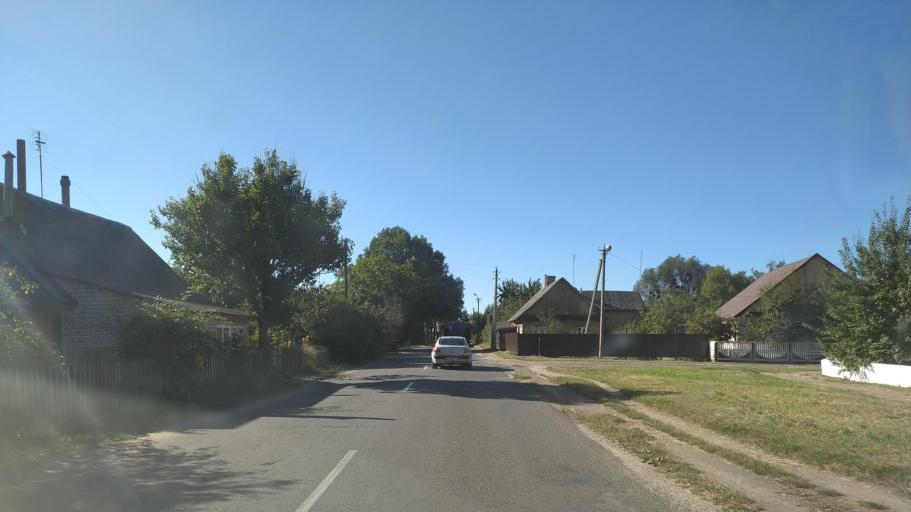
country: BY
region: Brest
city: Pruzhany
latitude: 52.4867
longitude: 24.7076
